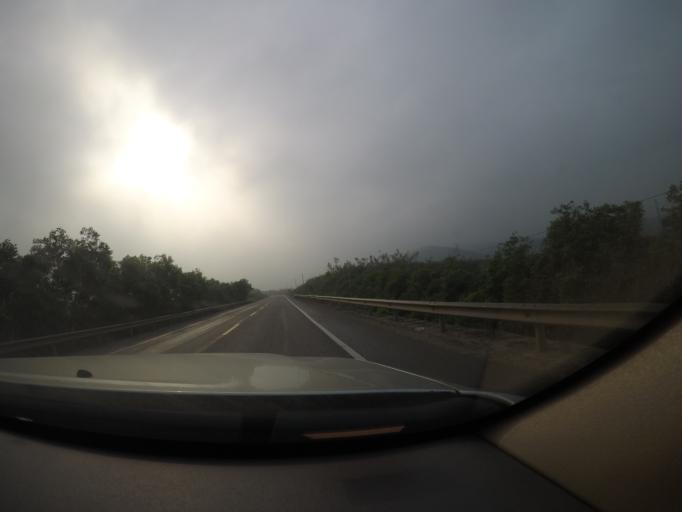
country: VN
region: Ha Tinh
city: Ky Anh
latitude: 18.0417
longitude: 106.2907
